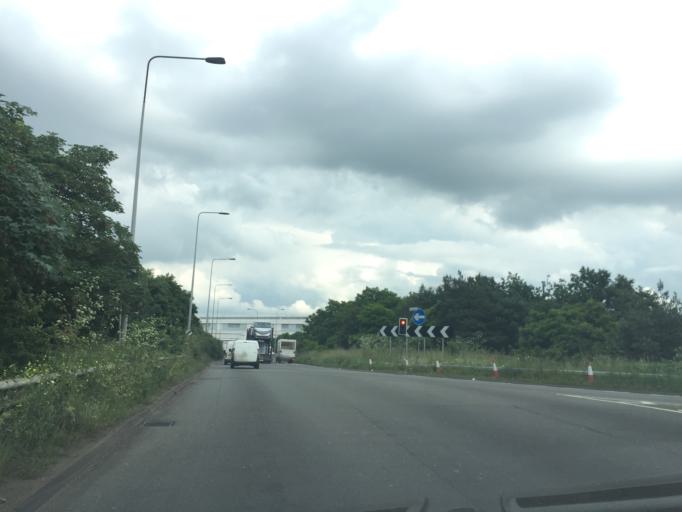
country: GB
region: England
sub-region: Hertfordshire
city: Waltham Cross
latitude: 51.6835
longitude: -0.0511
